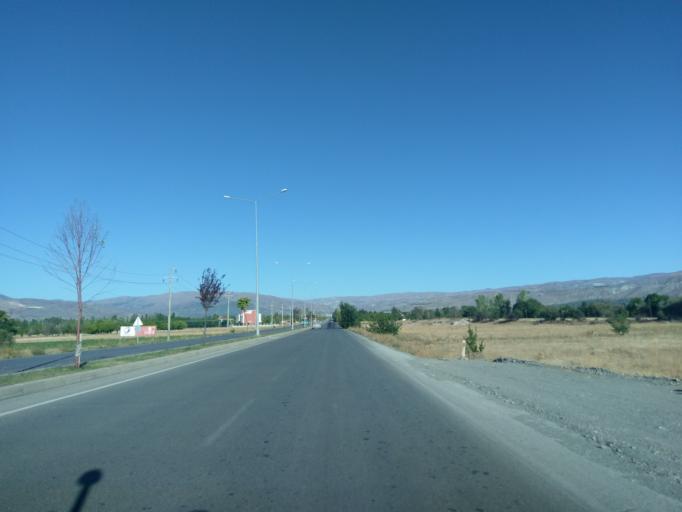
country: TR
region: Erzincan
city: Erzincan
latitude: 39.7661
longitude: 39.4331
